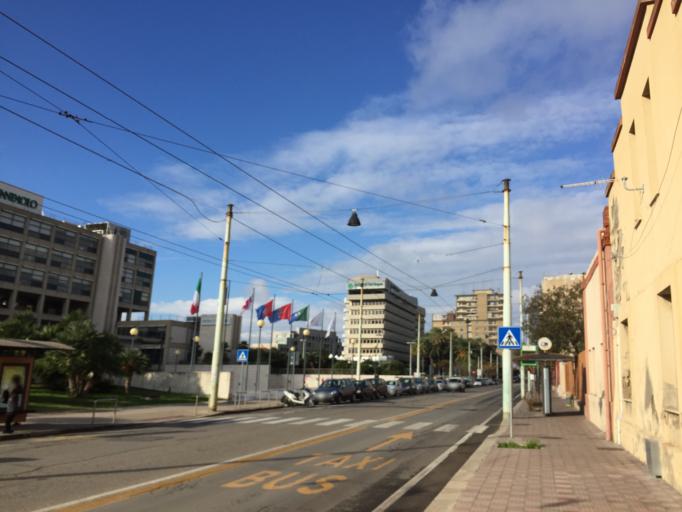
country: IT
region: Sardinia
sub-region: Provincia di Cagliari
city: Cagliari
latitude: 39.2101
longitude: 9.1226
